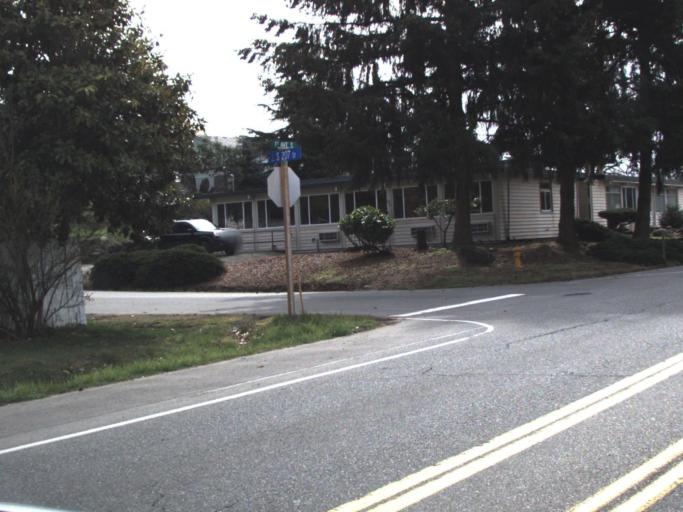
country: US
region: Washington
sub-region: King County
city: Des Moines
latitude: 47.4175
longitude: -122.3353
